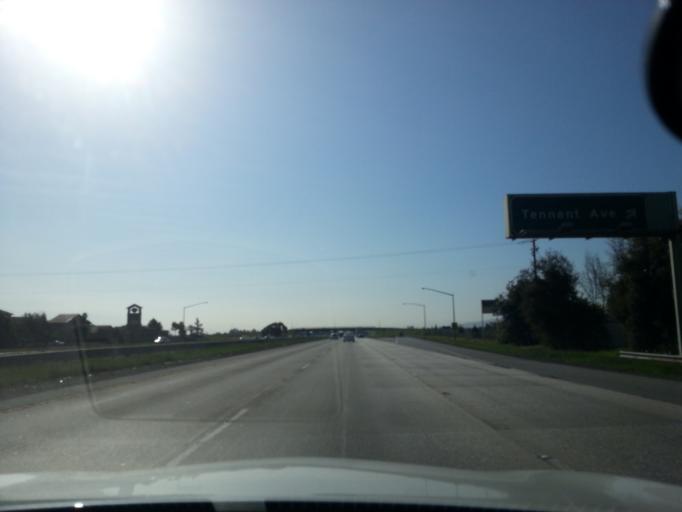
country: US
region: California
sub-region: Santa Clara County
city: Morgan Hill
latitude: 37.1241
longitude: -121.6293
